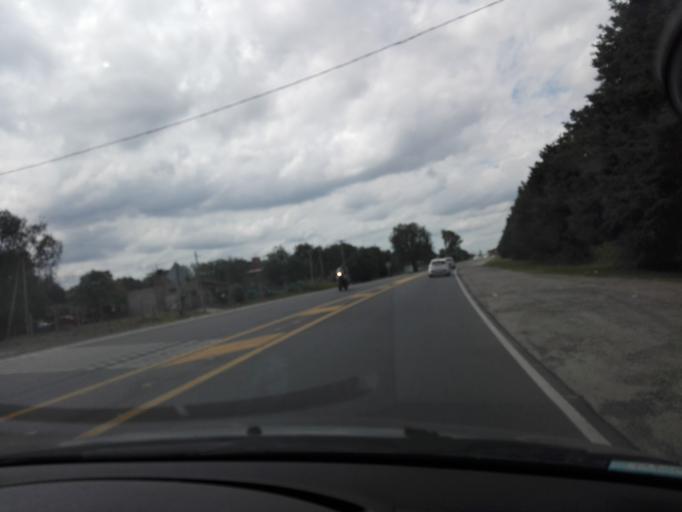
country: AR
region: Cordoba
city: Alta Gracia
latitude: -31.6338
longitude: -64.4358
